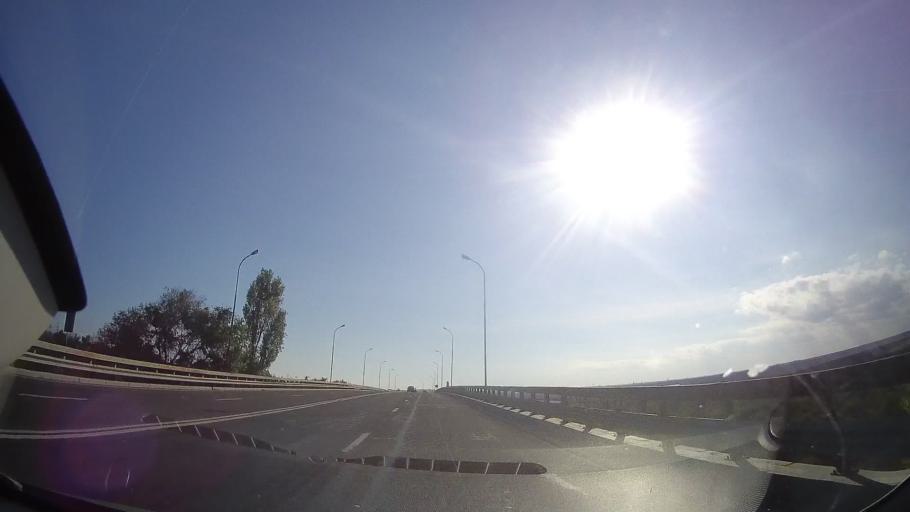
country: RO
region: Constanta
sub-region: Comuna Douazeci si Trei August
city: Dulcesti
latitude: 43.8590
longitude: 28.5757
